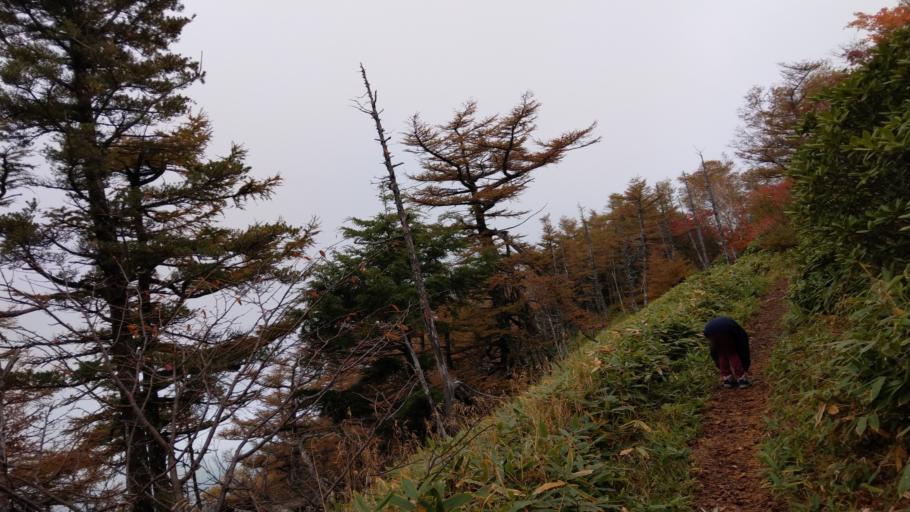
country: JP
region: Nagano
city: Komoro
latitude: 36.4018
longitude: 138.4574
